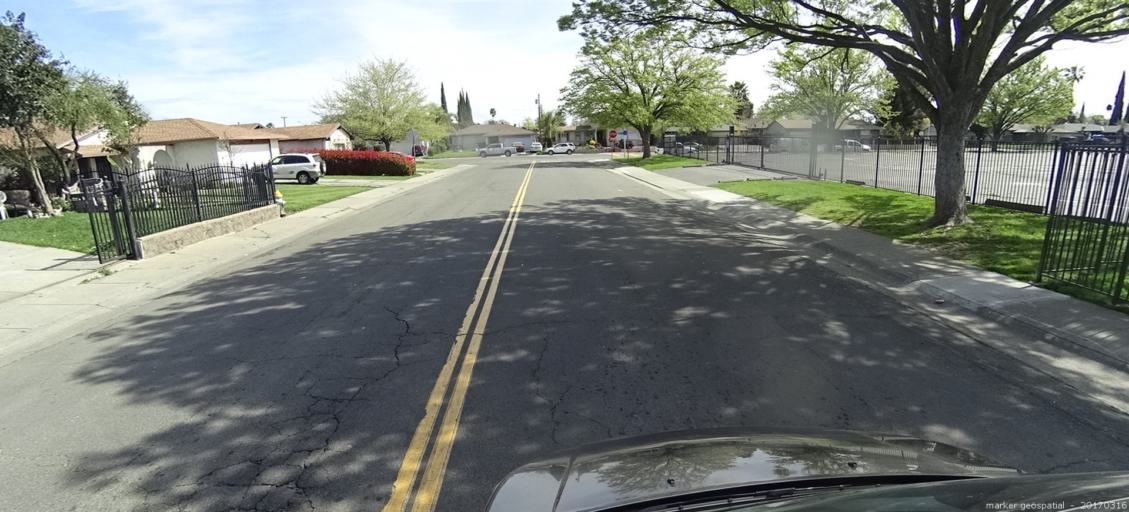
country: US
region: California
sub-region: Sacramento County
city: Parkway
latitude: 38.4773
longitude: -121.4812
